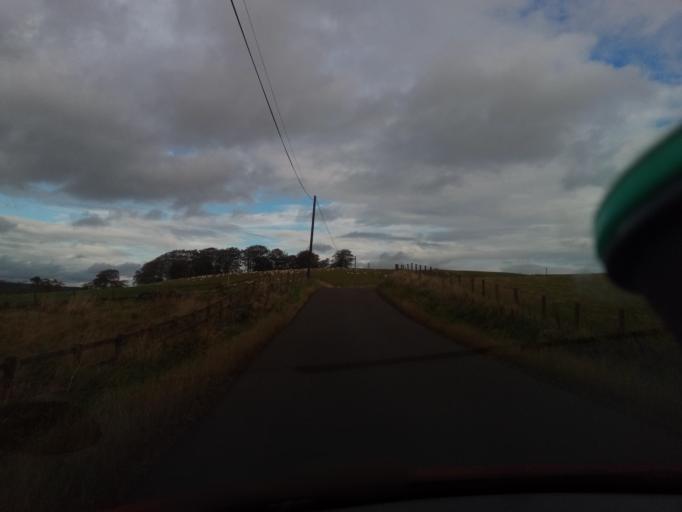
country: GB
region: Scotland
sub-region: South Lanarkshire
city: Carnwath
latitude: 55.7617
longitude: -3.6050
